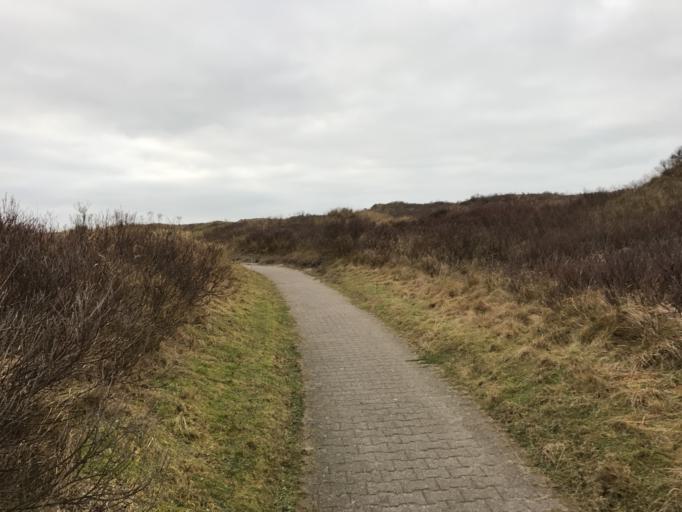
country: DE
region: Lower Saxony
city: Borkum
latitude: 53.6006
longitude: 6.6823
